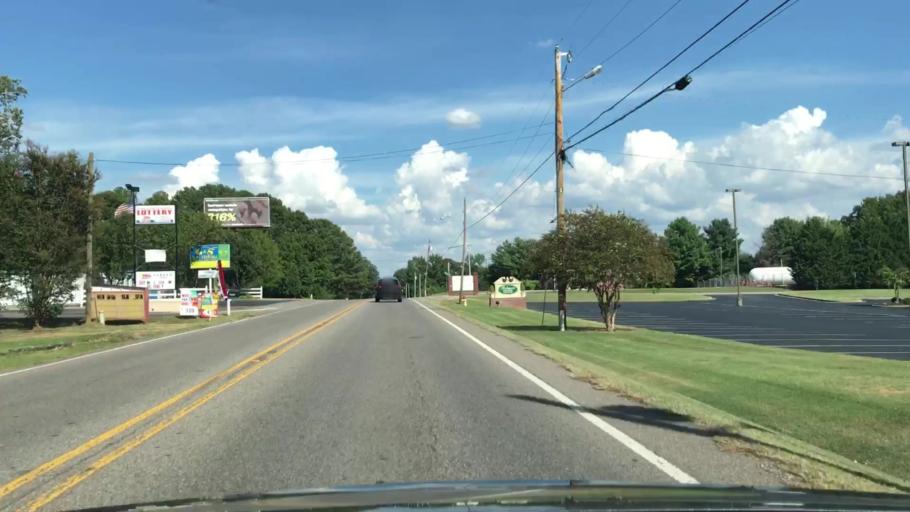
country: US
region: Tennessee
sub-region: Giles County
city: Ardmore
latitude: 34.9919
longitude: -86.8353
